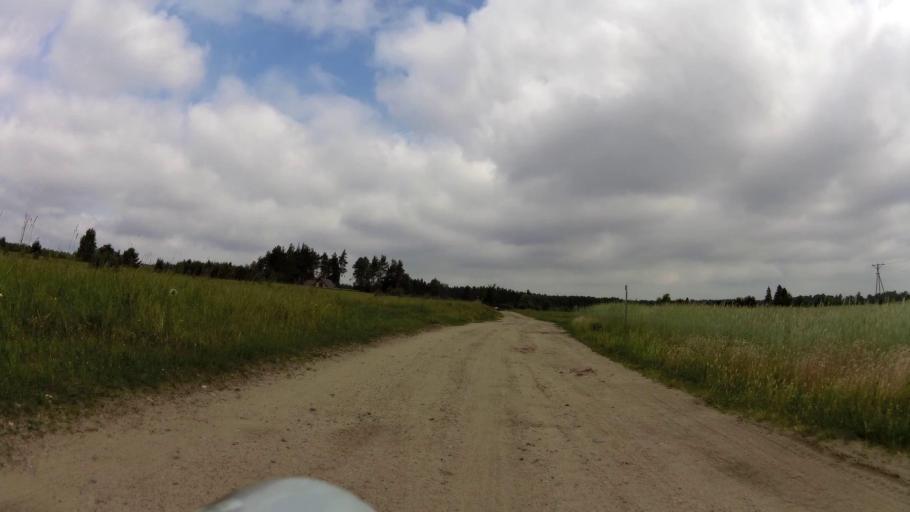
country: PL
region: West Pomeranian Voivodeship
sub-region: Powiat szczecinecki
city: Bialy Bor
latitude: 53.8942
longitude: 16.8267
